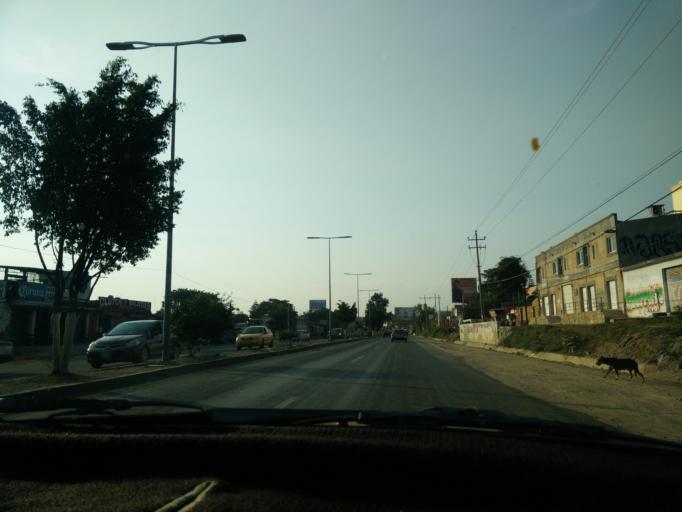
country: MX
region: Oaxaca
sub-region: Santa Maria Atzompa
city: San Jeronimo Yahuiche
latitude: 17.1108
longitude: -96.7556
